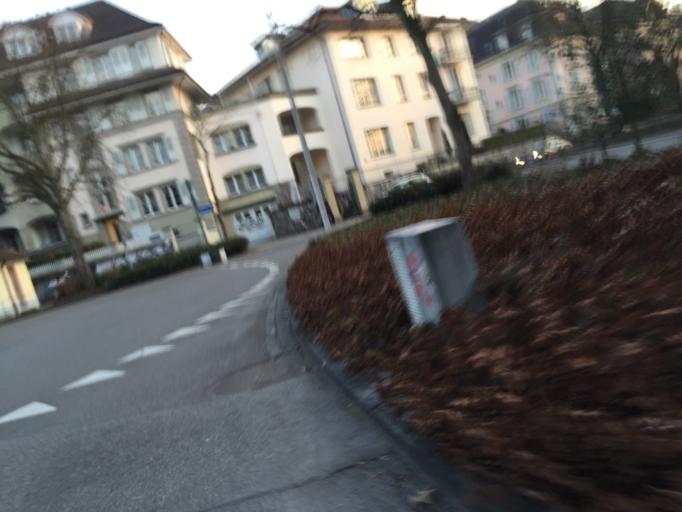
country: CH
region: Bern
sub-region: Bern-Mittelland District
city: Bern
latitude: 46.9522
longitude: 7.4309
